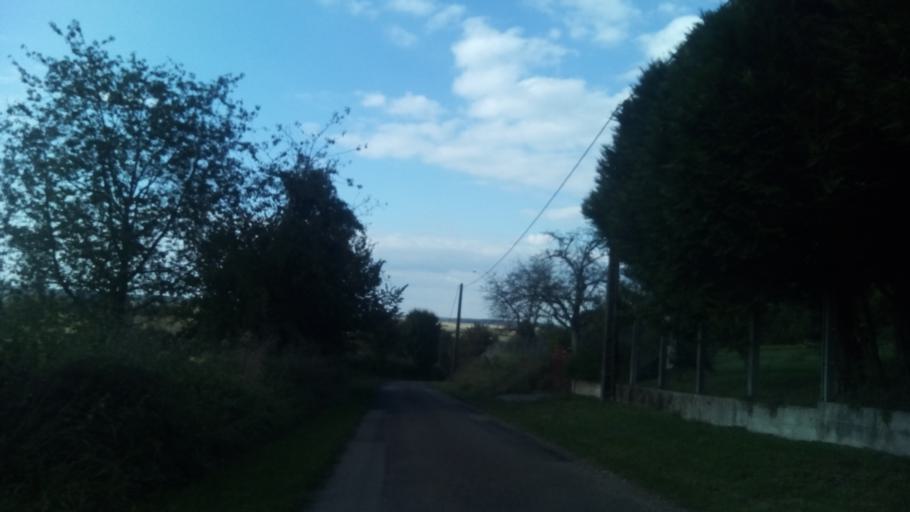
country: FR
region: Franche-Comte
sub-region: Departement de la Haute-Saone
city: Gy
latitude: 47.4176
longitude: 5.8538
